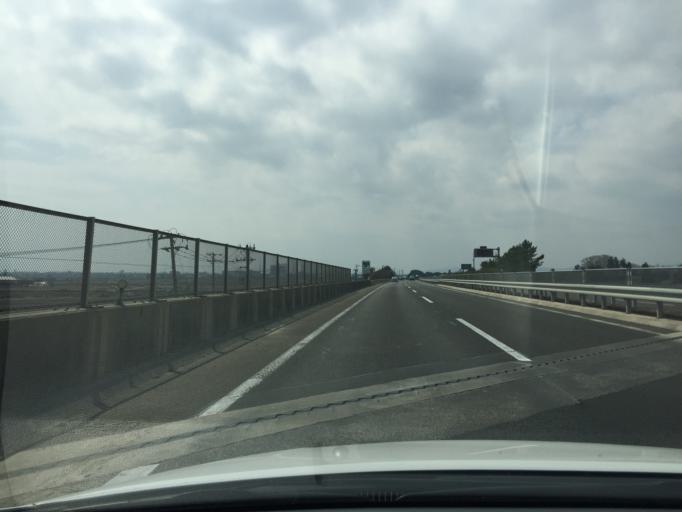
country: JP
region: Miyagi
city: Sendai
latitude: 38.1788
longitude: 140.9290
